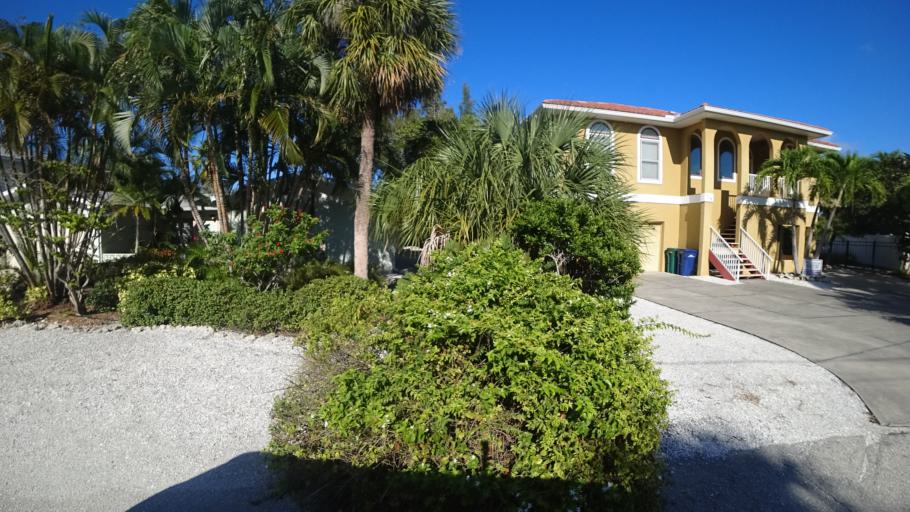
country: US
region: Florida
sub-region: Manatee County
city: Anna Maria
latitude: 27.5324
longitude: -82.7389
